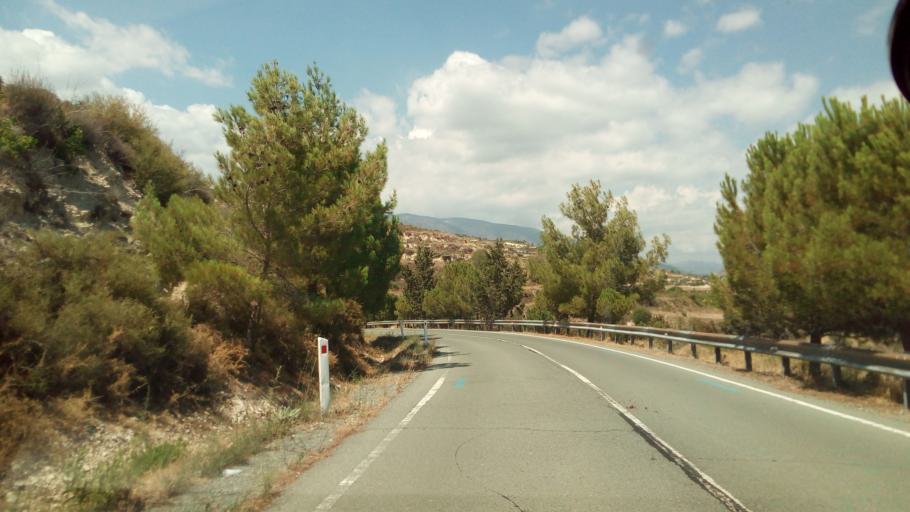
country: CY
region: Limassol
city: Pachna
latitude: 34.8293
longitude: 32.8458
